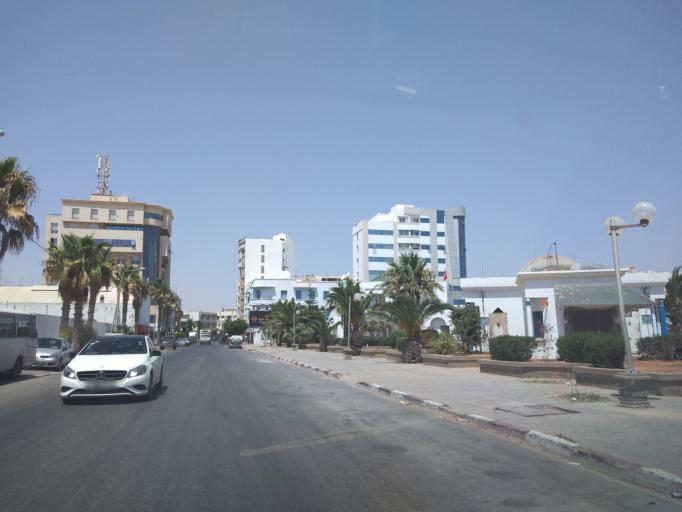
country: TN
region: Safaqis
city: Sfax
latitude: 34.7282
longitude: 10.7618
